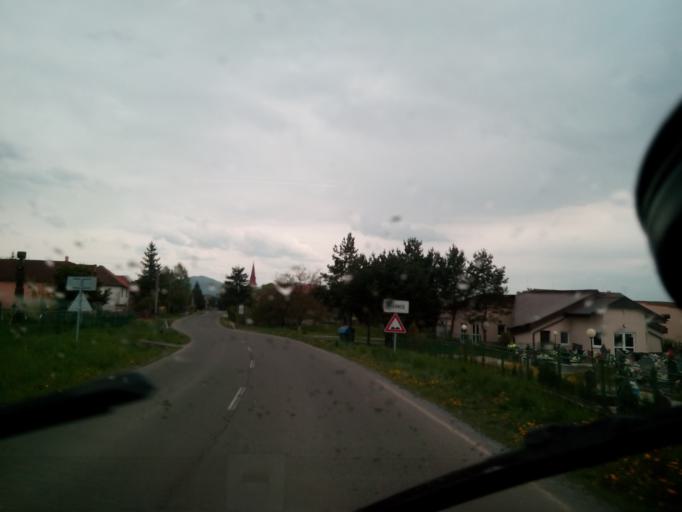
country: SK
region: Kosicky
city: Kosice
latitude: 48.7450
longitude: 21.4389
